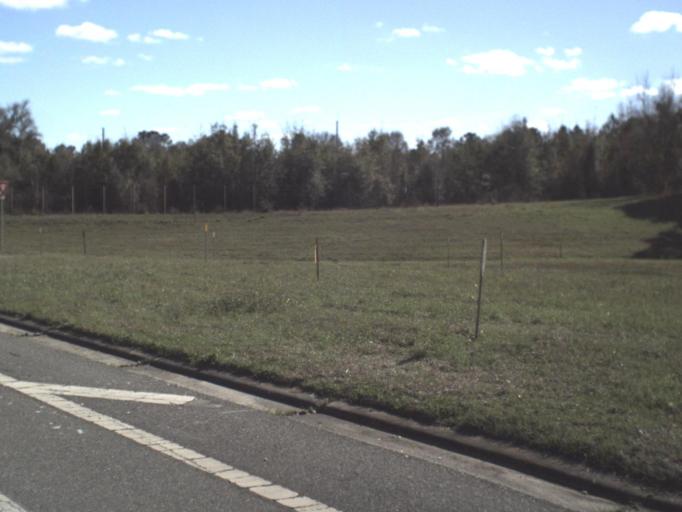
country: US
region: Florida
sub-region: Gadsden County
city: Midway
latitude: 30.4881
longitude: -84.4248
